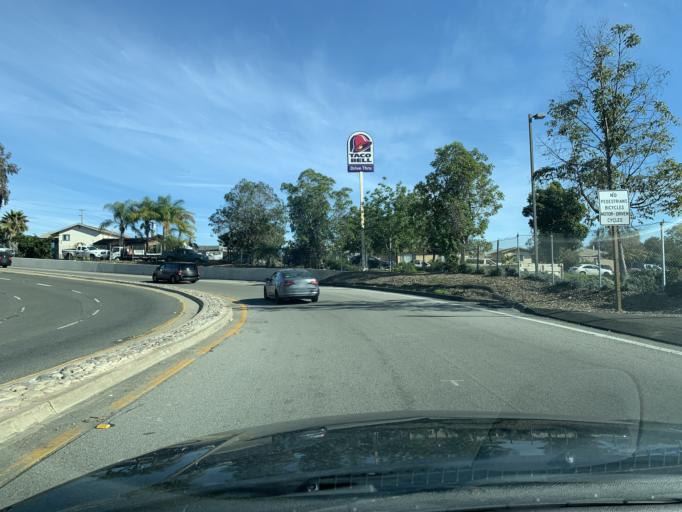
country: US
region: California
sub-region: San Diego County
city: Lemon Grove
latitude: 32.7438
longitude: -117.0424
